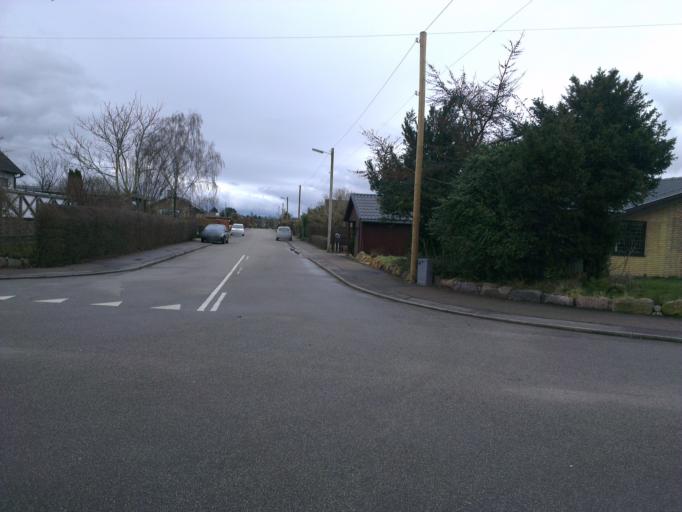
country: DK
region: Capital Region
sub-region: Frederikssund Kommune
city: Frederikssund
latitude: 55.8251
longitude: 12.0649
